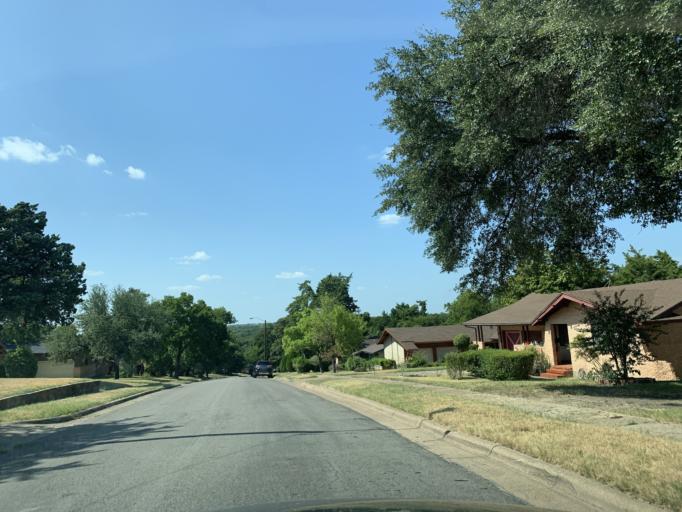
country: US
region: Texas
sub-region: Dallas County
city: Hutchins
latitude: 32.6779
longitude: -96.8020
